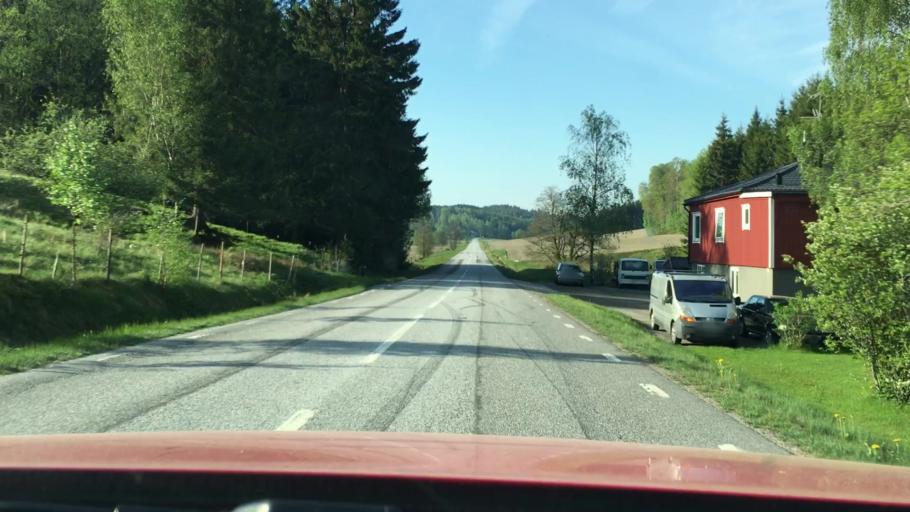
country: SE
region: Vaestra Goetaland
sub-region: Munkedals Kommun
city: Munkedal
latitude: 58.6145
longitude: 11.5587
